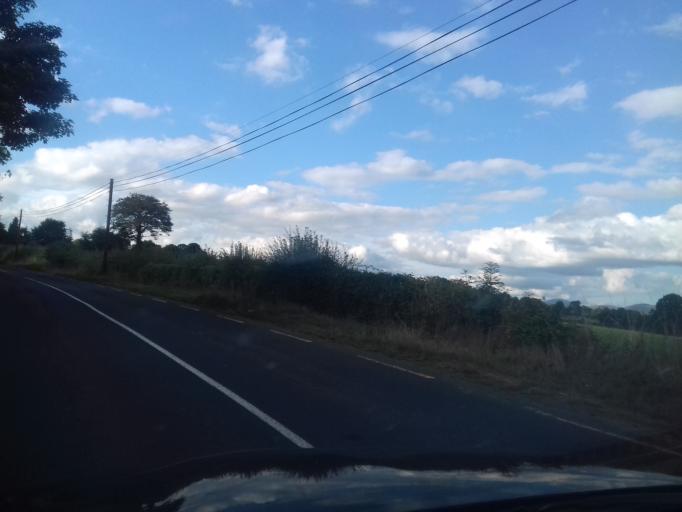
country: IE
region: Leinster
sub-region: Loch Garman
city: New Ross
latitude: 52.4410
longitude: -6.9606
